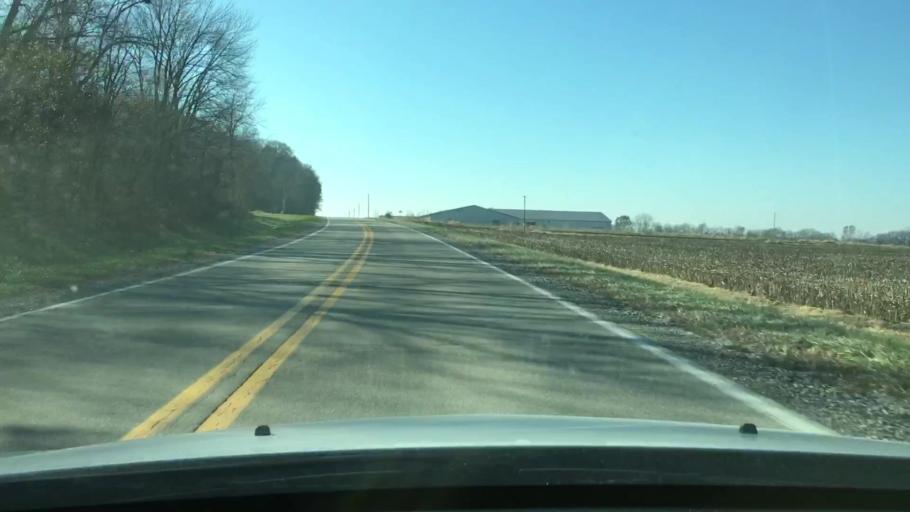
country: US
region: Illinois
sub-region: Morgan County
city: Meredosia
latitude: 39.7336
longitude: -90.5625
